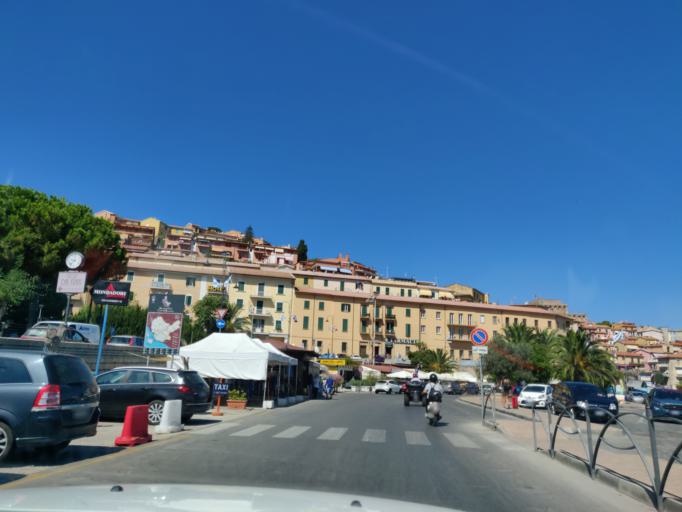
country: IT
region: Tuscany
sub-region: Provincia di Grosseto
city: Monte Argentario
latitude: 42.4352
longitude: 11.1215
